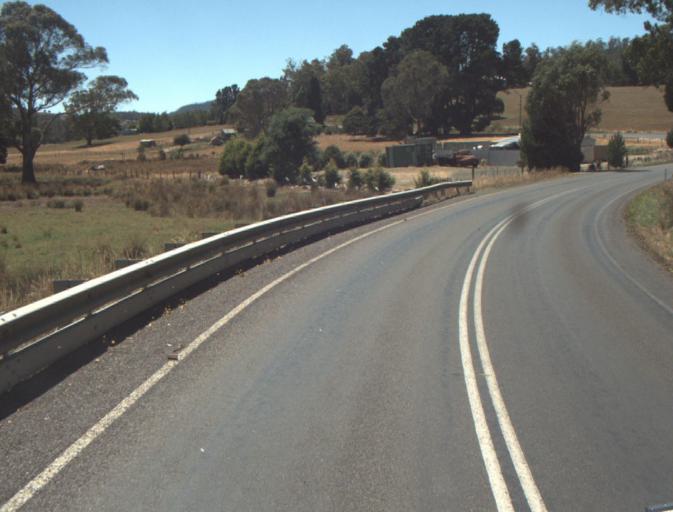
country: AU
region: Tasmania
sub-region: Launceston
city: Newstead
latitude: -41.3283
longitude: 147.3543
